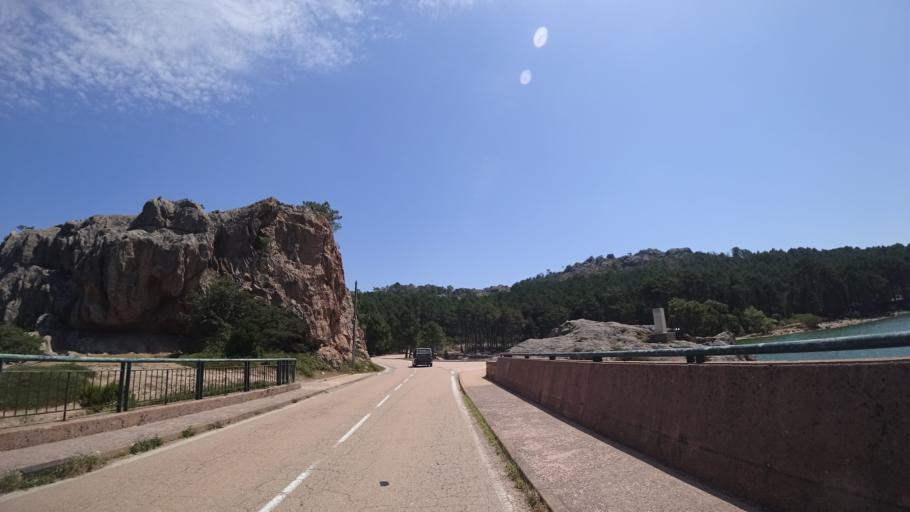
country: FR
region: Corsica
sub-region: Departement de la Corse-du-Sud
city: Zonza
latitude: 41.6683
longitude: 9.2080
